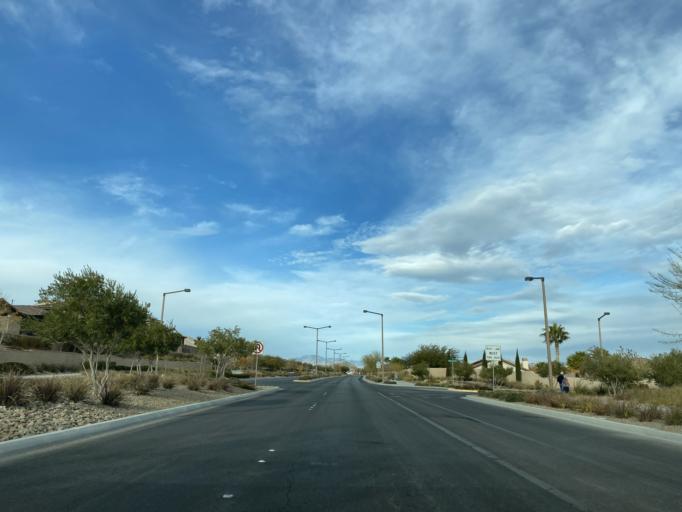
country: US
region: Nevada
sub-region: Clark County
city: Summerlin South
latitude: 36.1769
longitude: -115.3549
